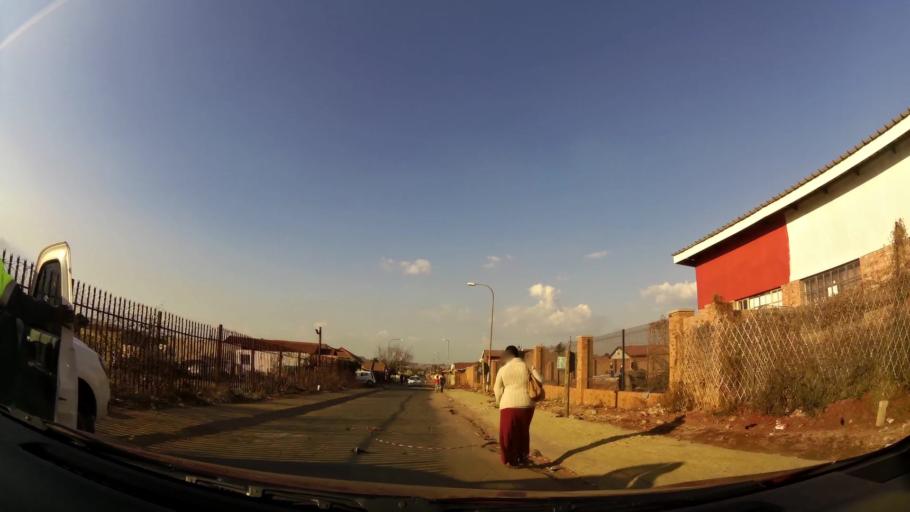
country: ZA
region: Gauteng
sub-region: City of Johannesburg Metropolitan Municipality
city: Soweto
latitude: -26.2273
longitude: 27.8551
